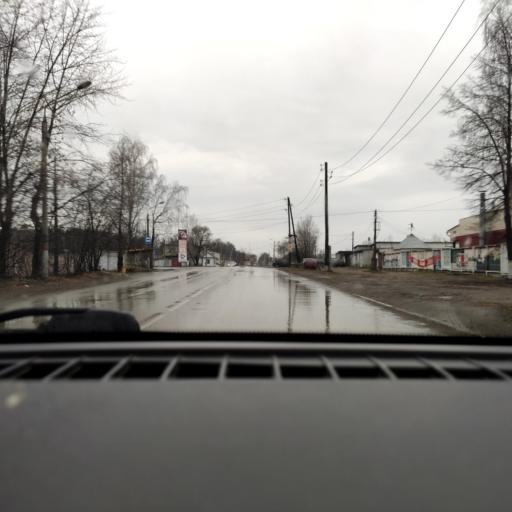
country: RU
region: Perm
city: Kultayevo
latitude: 57.9924
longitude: 55.9289
